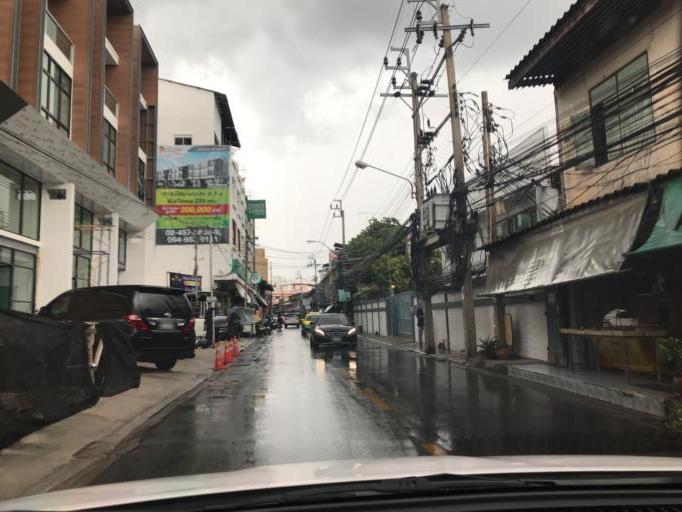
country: TH
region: Bangkok
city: Phasi Charoen
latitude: 13.7161
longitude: 100.4441
